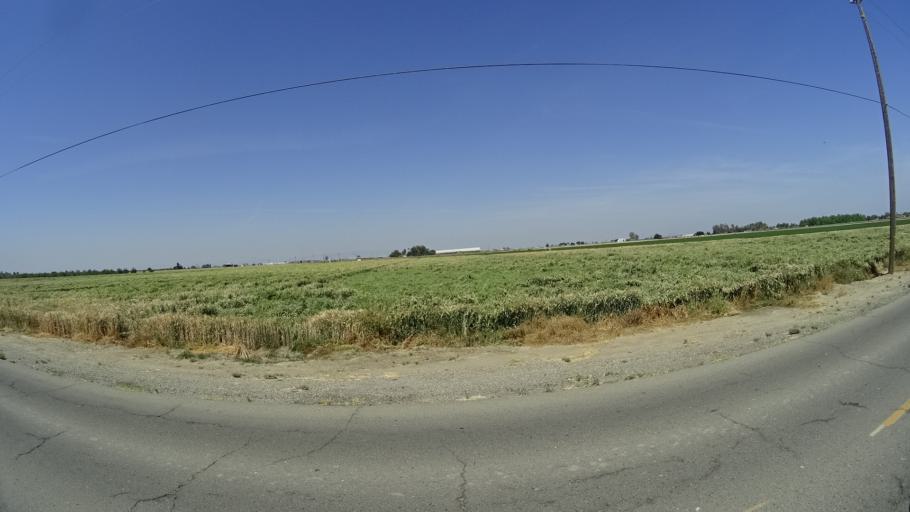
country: US
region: California
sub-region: Fresno County
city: Riverdale
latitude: 36.4155
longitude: -119.8513
